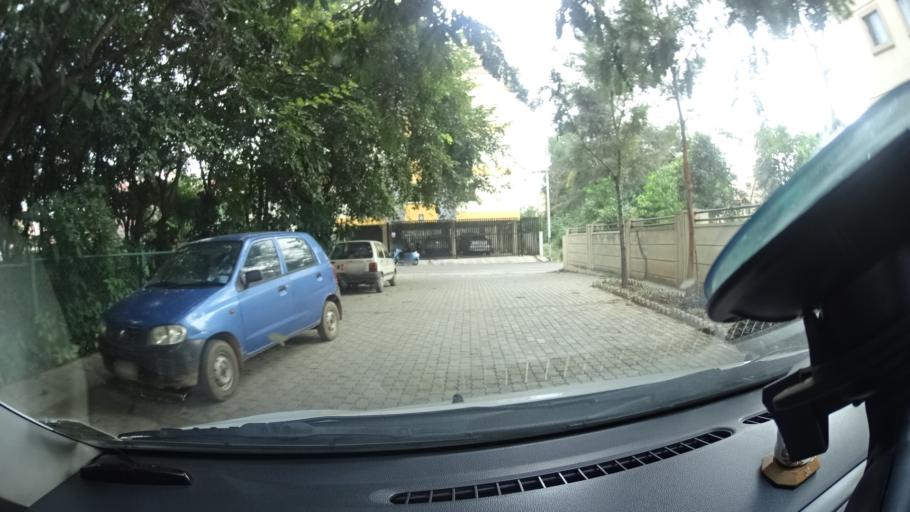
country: IN
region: Karnataka
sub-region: Bangalore Urban
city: Yelahanka
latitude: 13.0935
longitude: 77.5863
